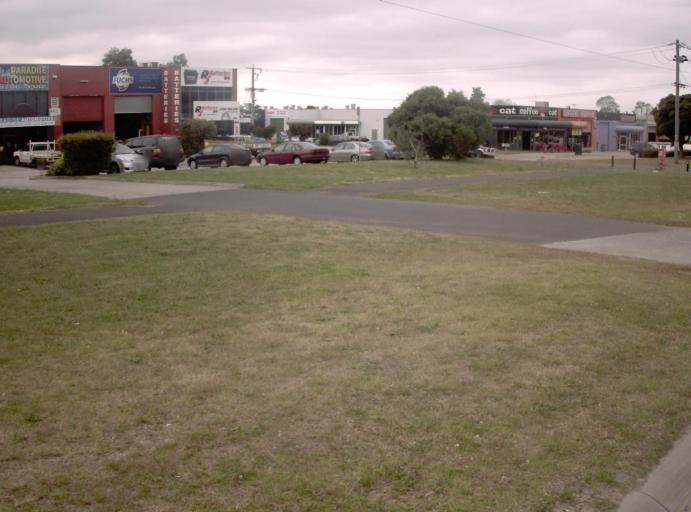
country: AU
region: Victoria
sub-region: Casey
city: Hallam
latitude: -38.0084
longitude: 145.2729
